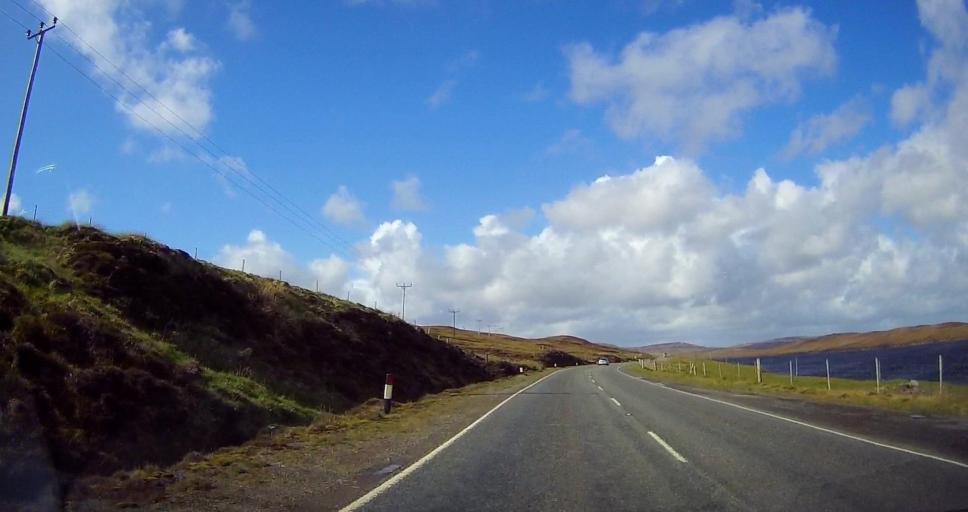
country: GB
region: Scotland
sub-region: Shetland Islands
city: Lerwick
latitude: 60.2448
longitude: -1.2286
